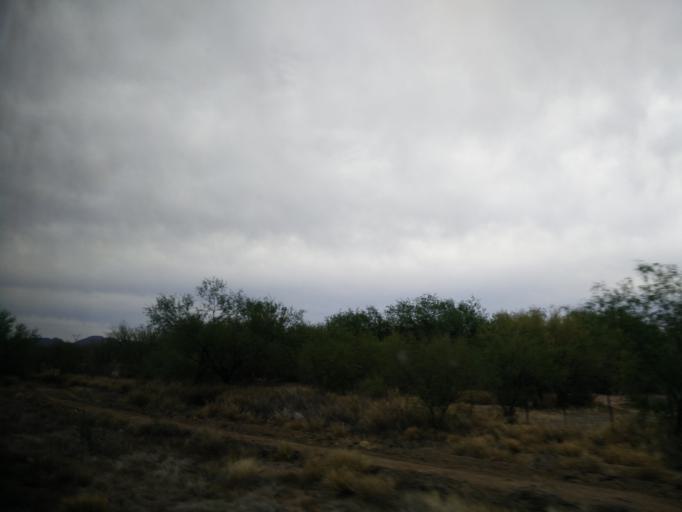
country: MX
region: Sonora
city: Hermosillo
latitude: 28.7054
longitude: -110.9854
